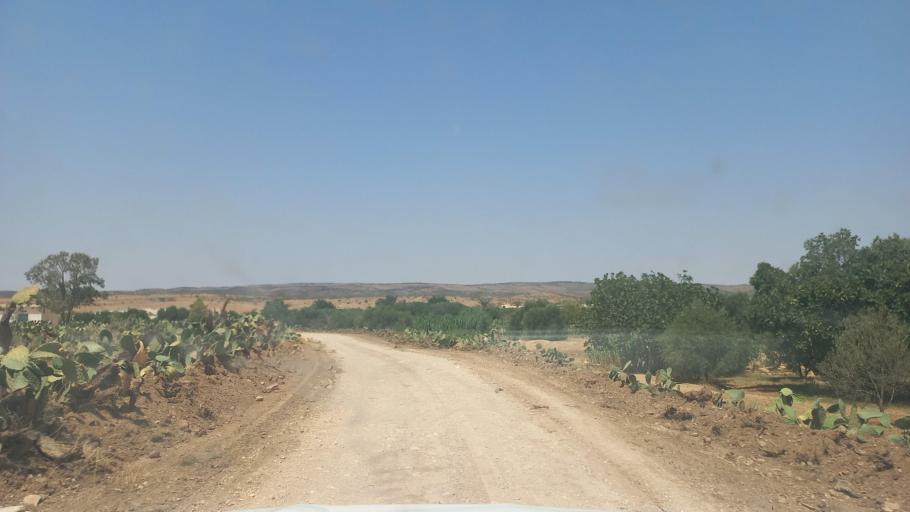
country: TN
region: Al Qasrayn
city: Kasserine
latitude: 35.2943
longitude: 8.9468
